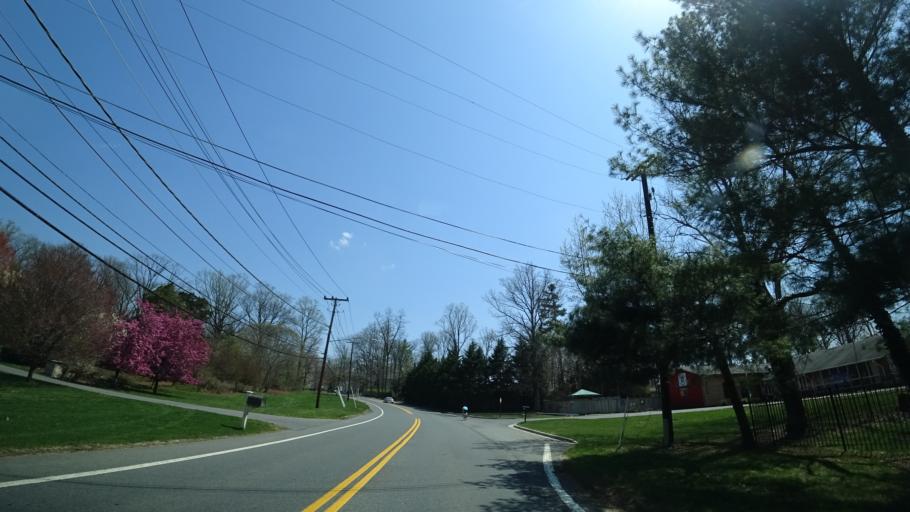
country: US
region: Maryland
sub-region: Montgomery County
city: Cabin John
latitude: 39.0057
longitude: -77.1467
